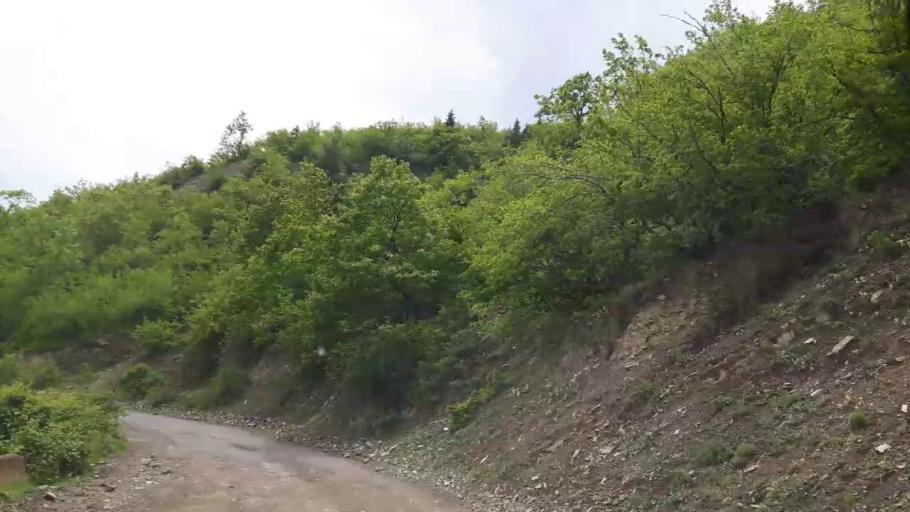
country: GE
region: Shida Kartli
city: Gori
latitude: 41.8859
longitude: 43.9978
